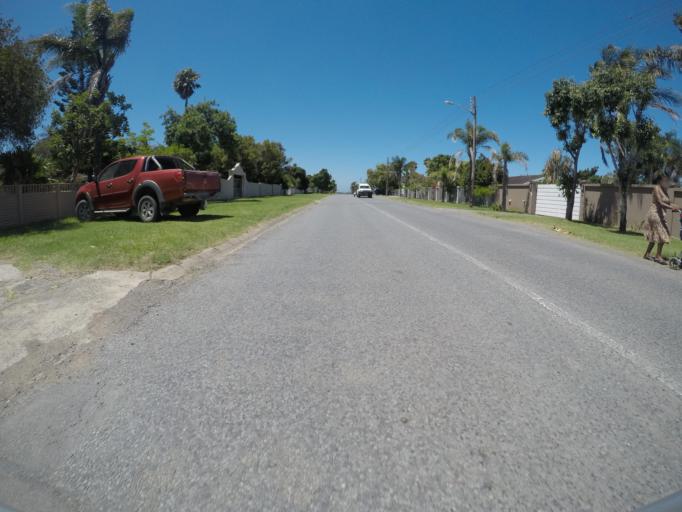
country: ZA
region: Eastern Cape
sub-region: Buffalo City Metropolitan Municipality
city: East London
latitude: -32.9580
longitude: 27.9386
